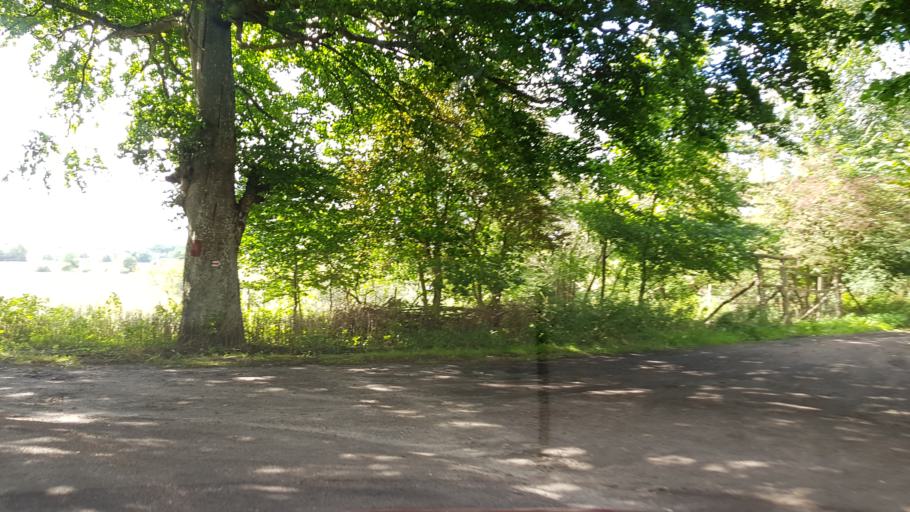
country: PL
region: West Pomeranian Voivodeship
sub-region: Powiat bialogardzki
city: Tychowo
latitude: 53.9917
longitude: 16.3029
